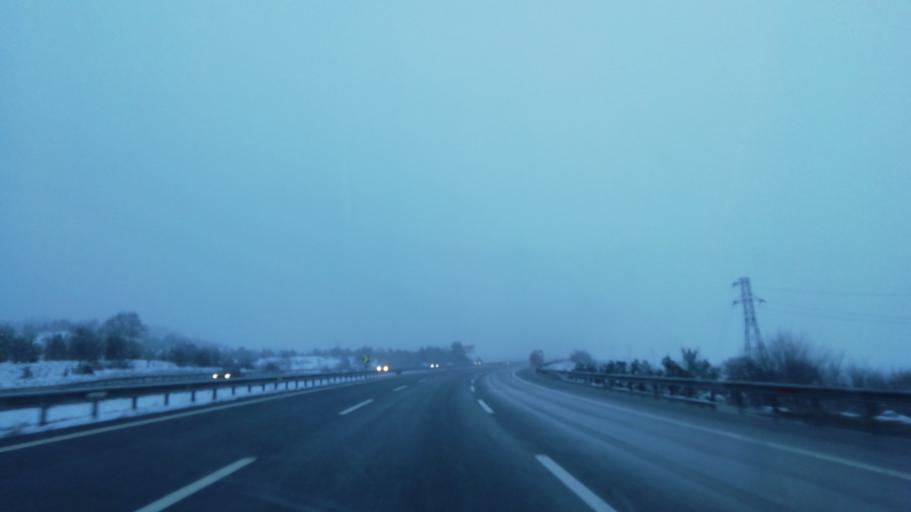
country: TR
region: Bolu
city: Bolu
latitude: 40.7610
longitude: 31.5893
